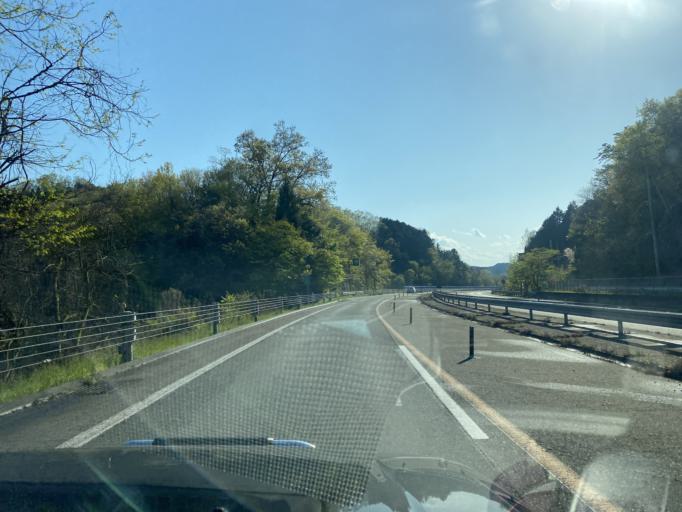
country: JP
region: Kyoto
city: Ayabe
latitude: 35.3232
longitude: 135.2499
